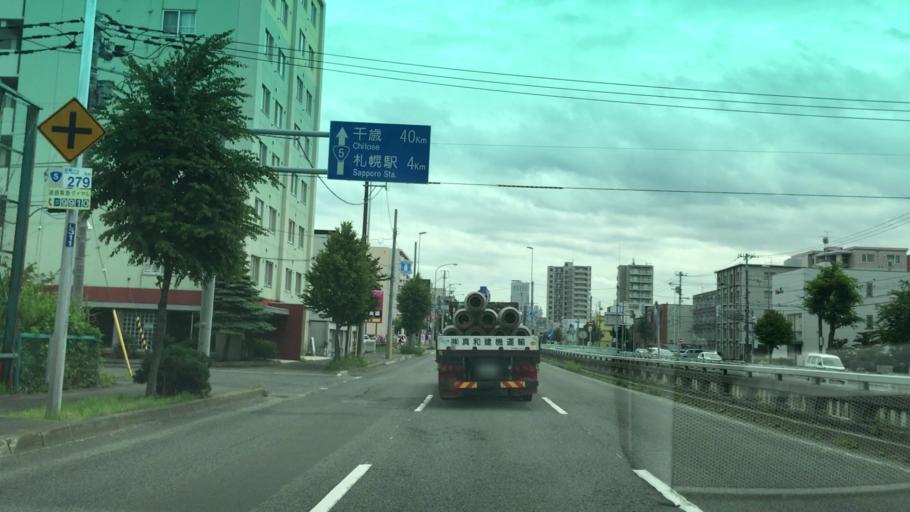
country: JP
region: Hokkaido
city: Sapporo
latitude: 43.0902
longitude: 141.3480
